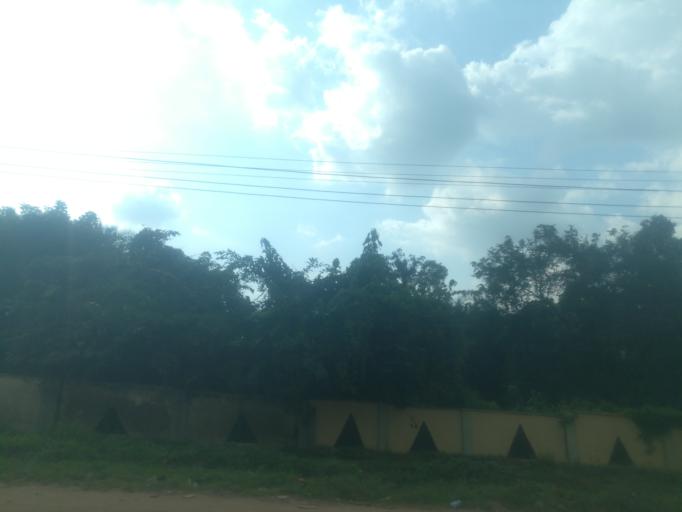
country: NG
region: Ogun
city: Abeokuta
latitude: 7.1243
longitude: 3.2985
